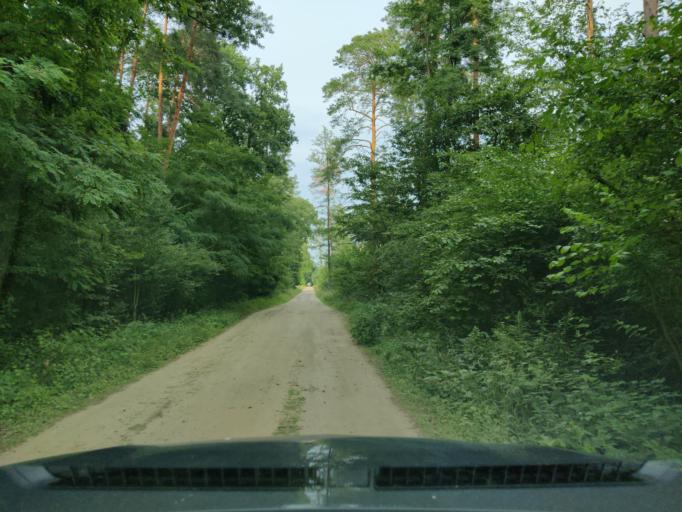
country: PL
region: Masovian Voivodeship
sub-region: Powiat pultuski
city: Obryte
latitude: 52.7021
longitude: 21.2183
